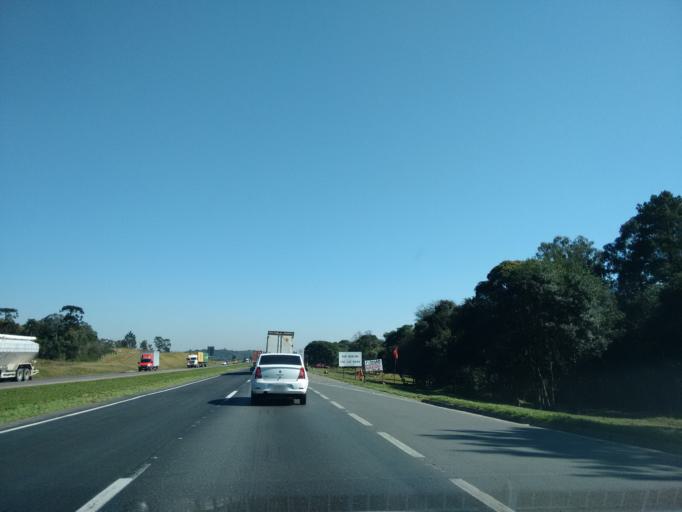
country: BR
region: Parana
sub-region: Sao Jose Dos Pinhais
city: Sao Jose dos Pinhais
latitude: -25.5695
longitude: -49.2223
